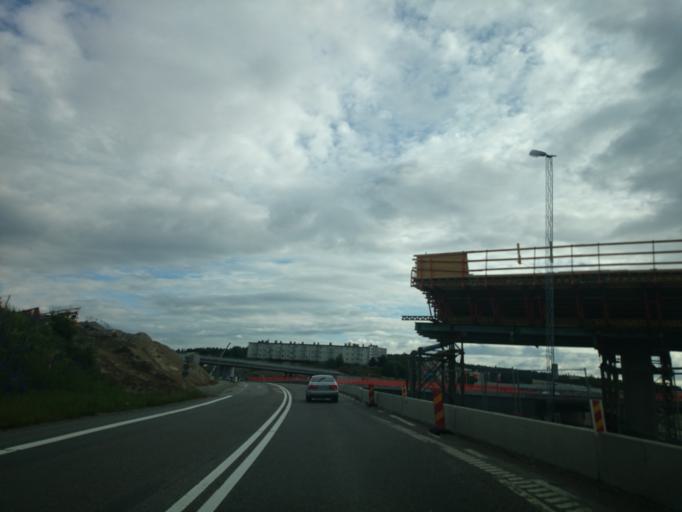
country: SE
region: Vaesternorrland
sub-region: Sundsvalls Kommun
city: Sundsvall
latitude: 62.3967
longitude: 17.3355
